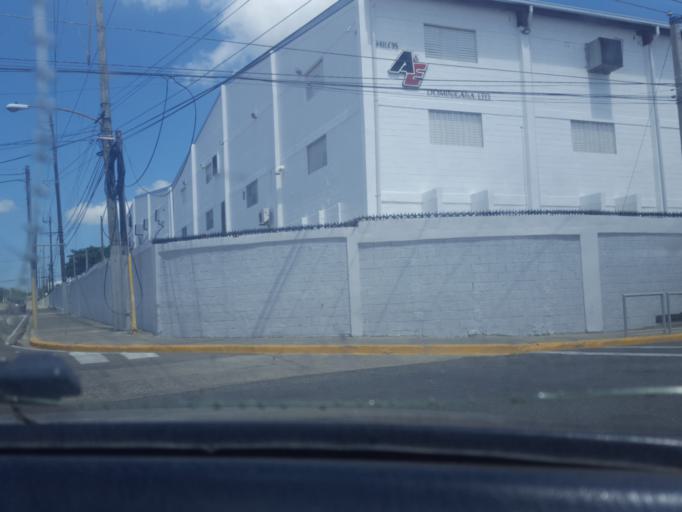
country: DO
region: Santiago
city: Santiago de los Caballeros
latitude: 19.4737
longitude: -70.7316
